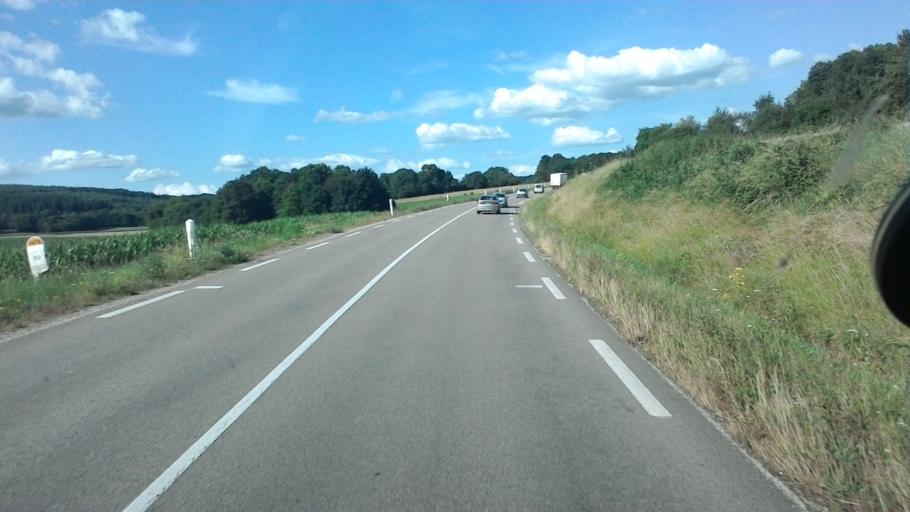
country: FR
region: Franche-Comte
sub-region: Departement de la Haute-Saone
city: Noidans-les-Vesoul
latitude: 47.5944
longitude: 6.1056
